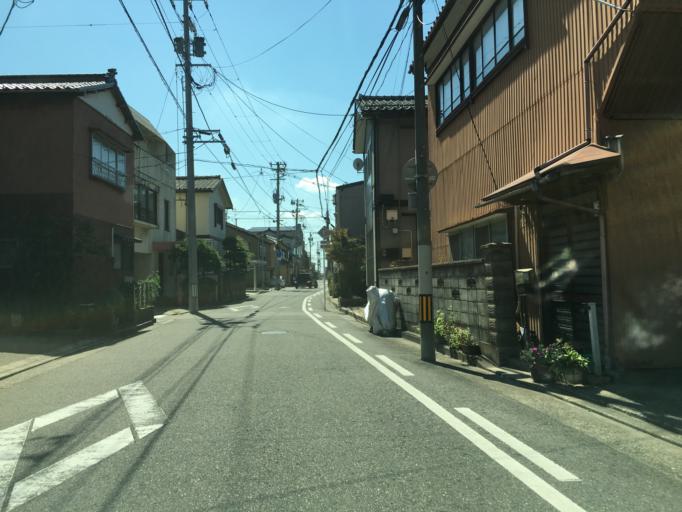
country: JP
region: Niigata
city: Niigata-shi
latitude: 37.9043
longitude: 139.0156
